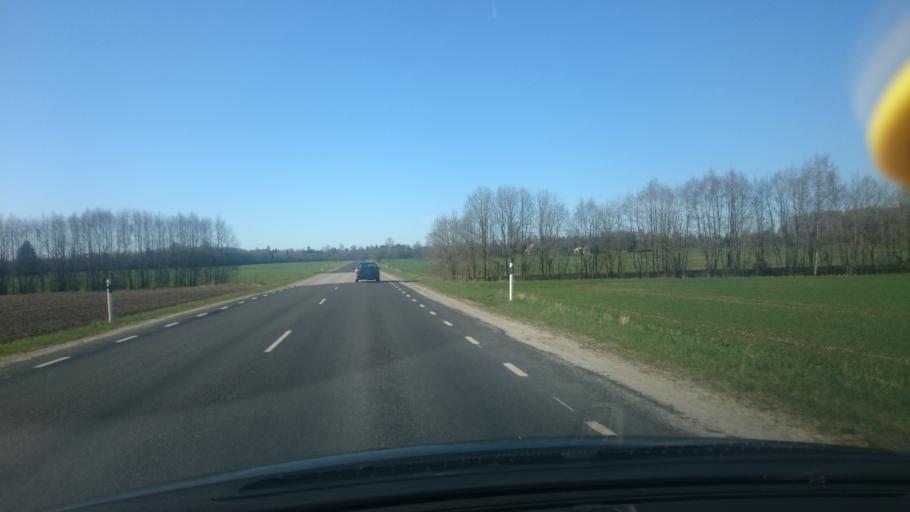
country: EE
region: Harju
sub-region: Raasiku vald
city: Raasiku
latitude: 59.1320
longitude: 25.2039
